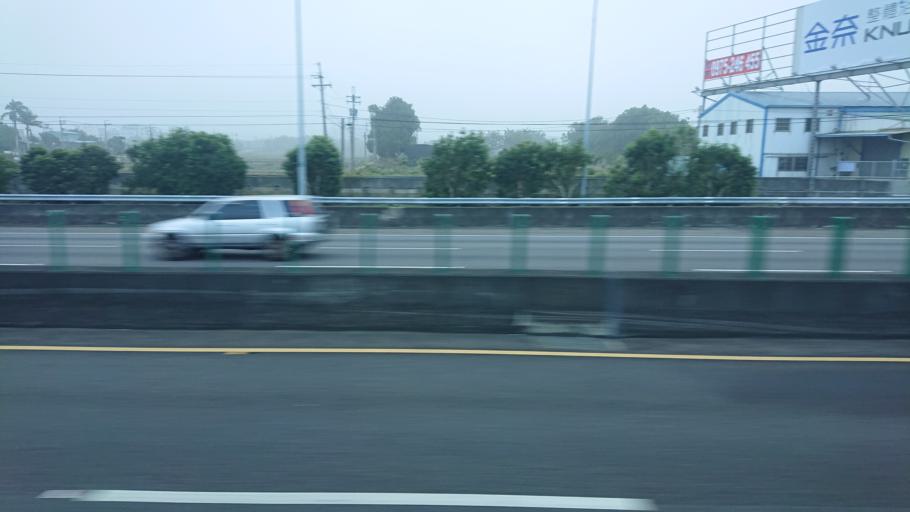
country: TW
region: Taiwan
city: Fengyuan
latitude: 24.3232
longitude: 120.7087
